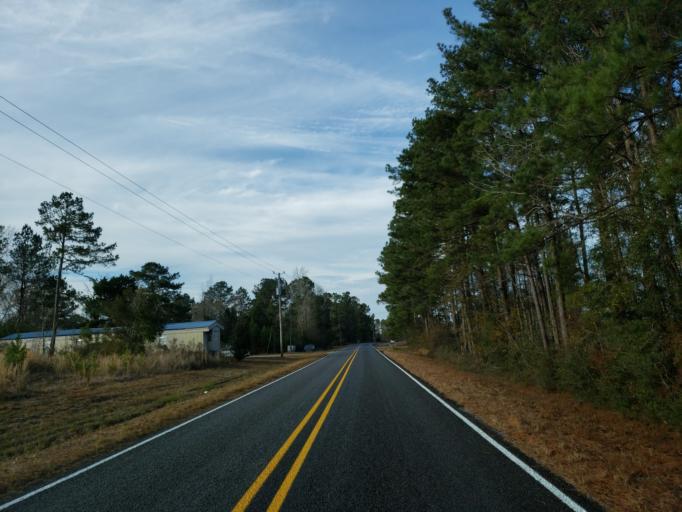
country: US
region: Mississippi
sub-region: Wayne County
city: Belmont
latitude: 31.4937
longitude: -88.5051
